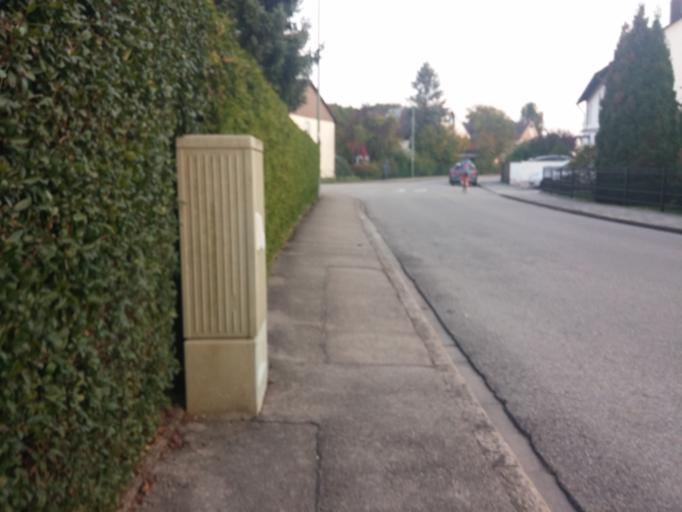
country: DE
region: Bavaria
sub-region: Upper Bavaria
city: Zorneding
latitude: 48.0944
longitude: 11.8425
